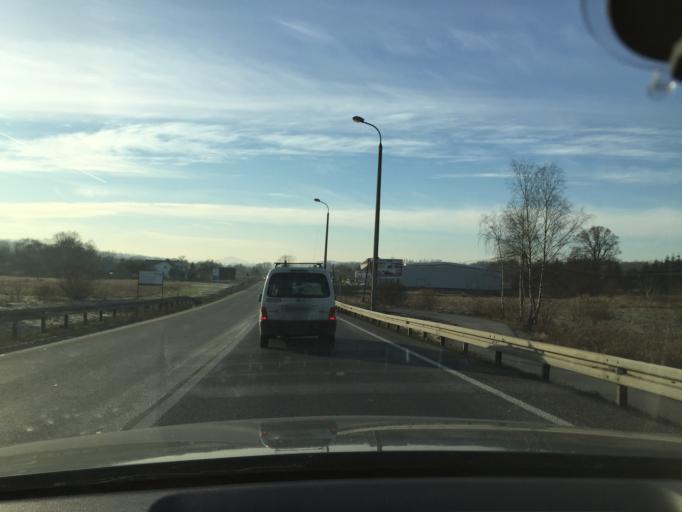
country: PL
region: Lesser Poland Voivodeship
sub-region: Powiat myslenicki
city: Glogoczow
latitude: 49.9071
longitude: 19.8631
